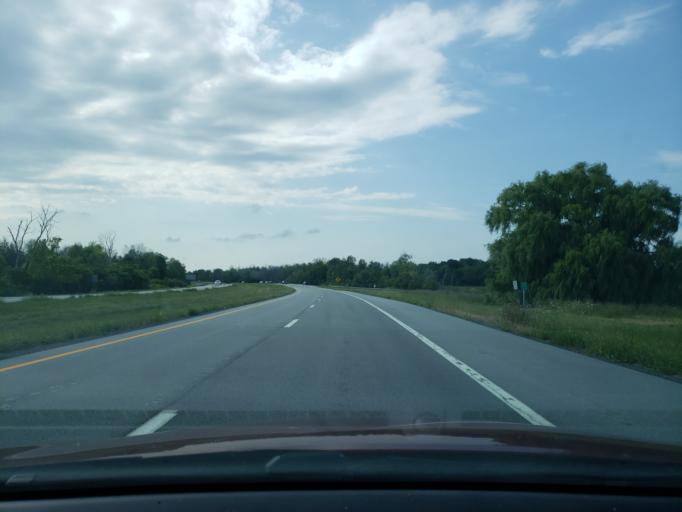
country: US
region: New York
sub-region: Monroe County
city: Greece
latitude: 43.2708
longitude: -77.6656
